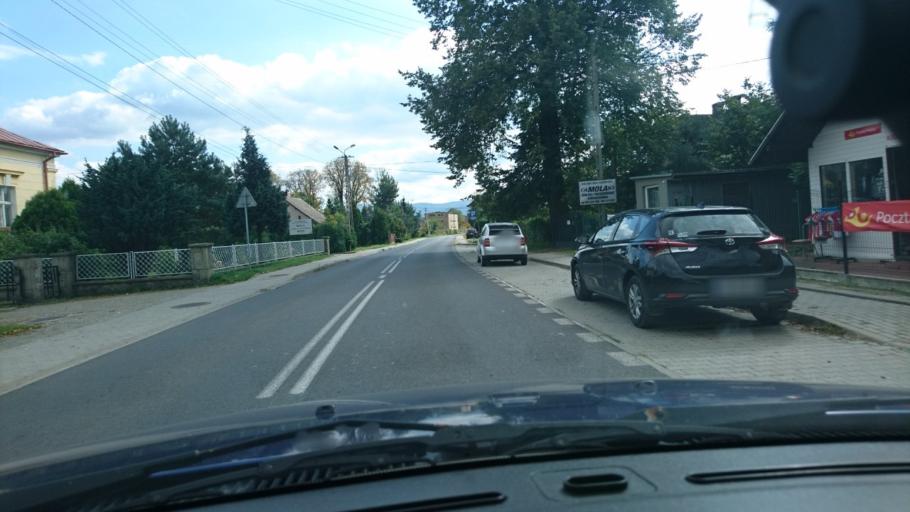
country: PL
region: Silesian Voivodeship
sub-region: Powiat bielski
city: Ligota
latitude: 49.8778
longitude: 18.9504
